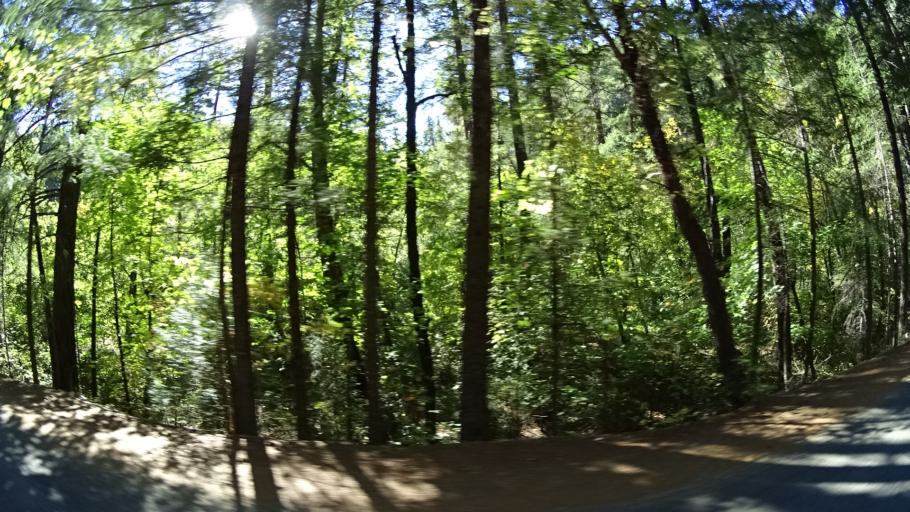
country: US
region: California
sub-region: Siskiyou County
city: Happy Camp
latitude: 41.3099
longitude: -123.1700
